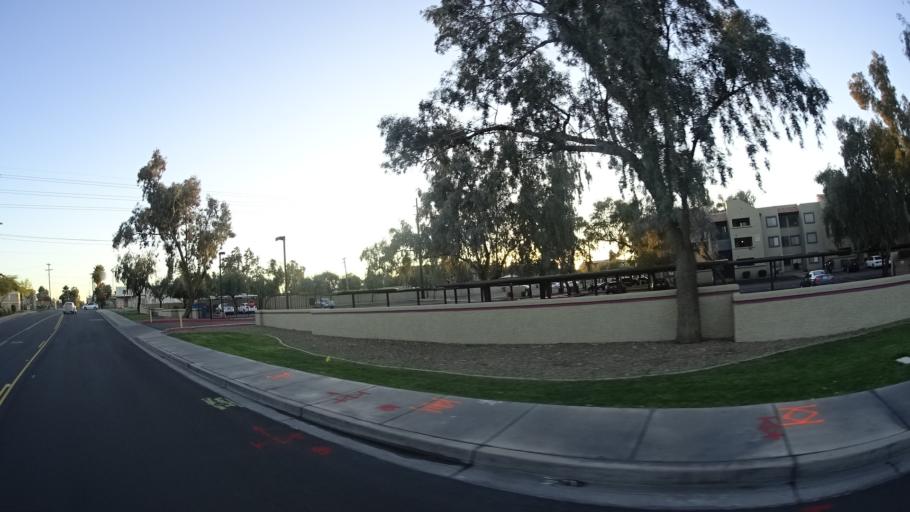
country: US
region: Arizona
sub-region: Maricopa County
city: Tempe
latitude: 33.4203
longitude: -111.9178
